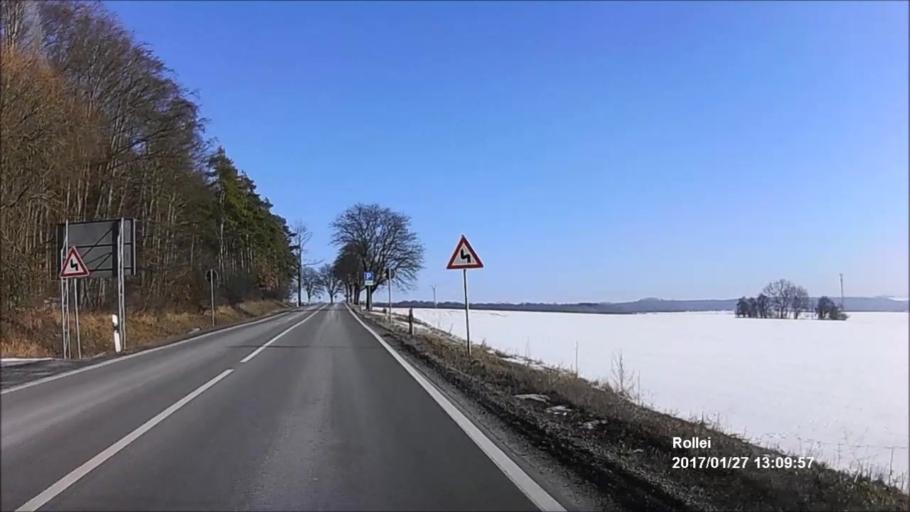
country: DE
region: Thuringia
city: Blankenburg
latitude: 51.2178
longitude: 10.7191
